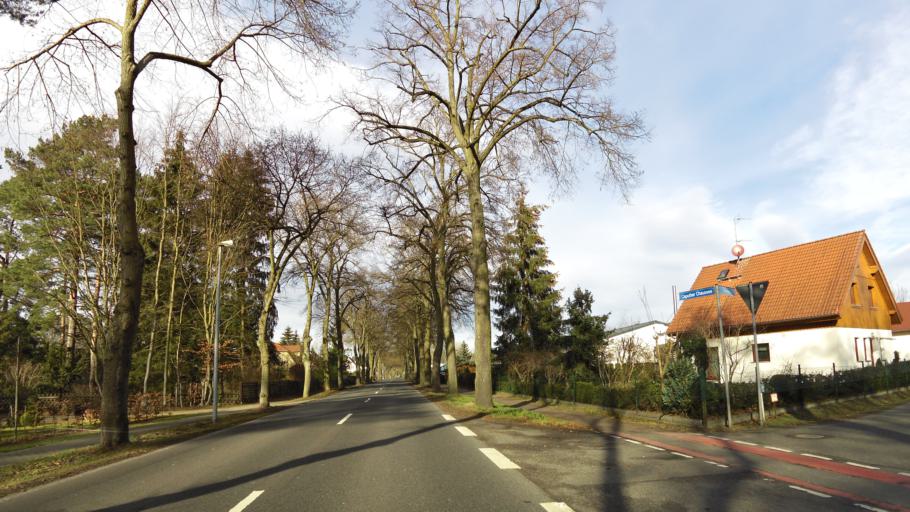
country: DE
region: Brandenburg
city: Michendorf
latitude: 52.3220
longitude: 13.0337
